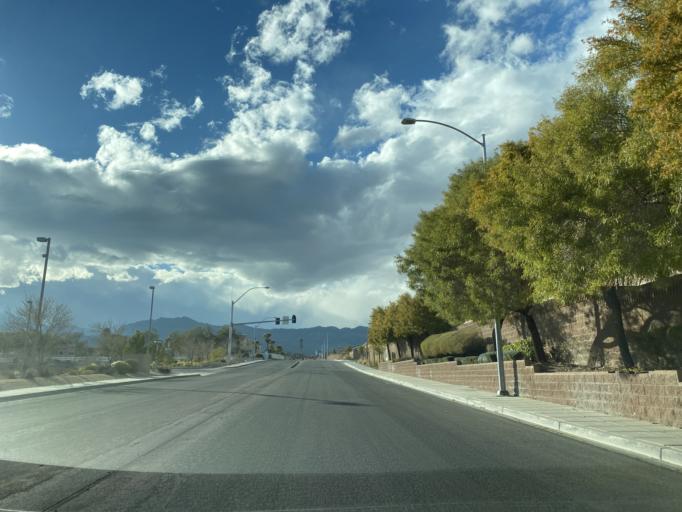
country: US
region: Nevada
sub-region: Clark County
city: Summerlin South
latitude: 36.2828
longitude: -115.3042
